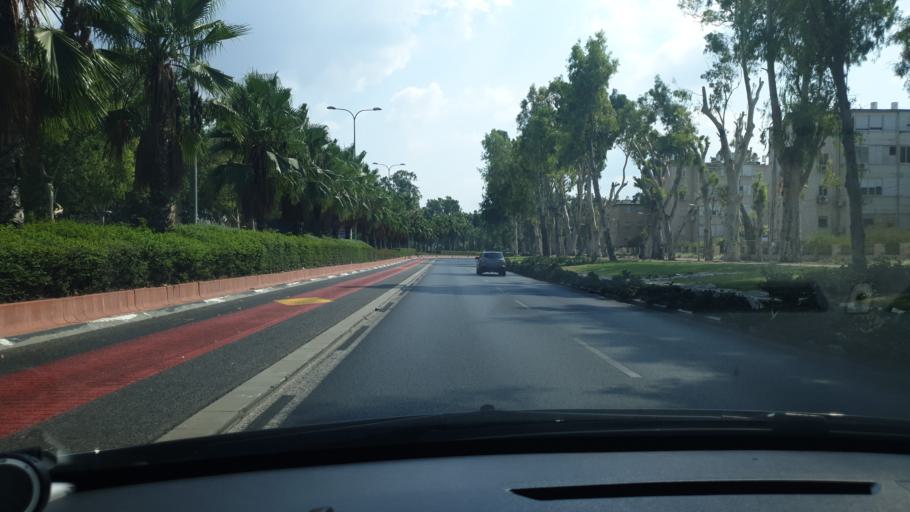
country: IL
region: Haifa
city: Qiryat Bialik
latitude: 32.8212
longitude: 35.0792
